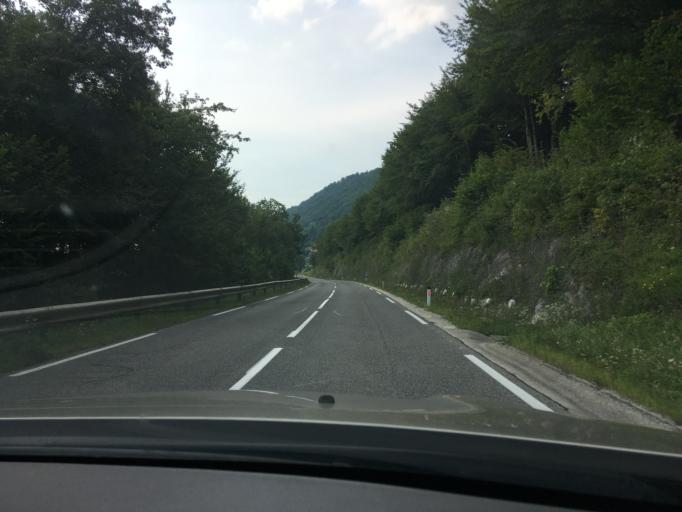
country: SI
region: Zuzemberk
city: Zuzemberk
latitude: 45.7915
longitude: 14.9886
